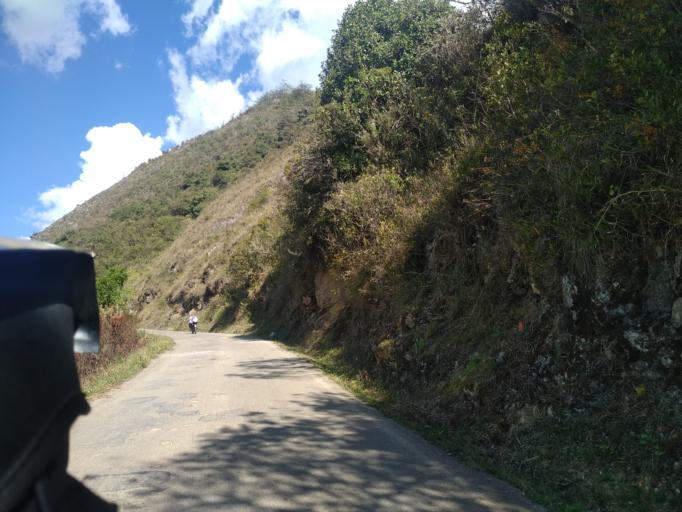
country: PE
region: Amazonas
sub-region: Provincia de Chachapoyas
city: Montevideo
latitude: -6.7141
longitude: -77.8165
